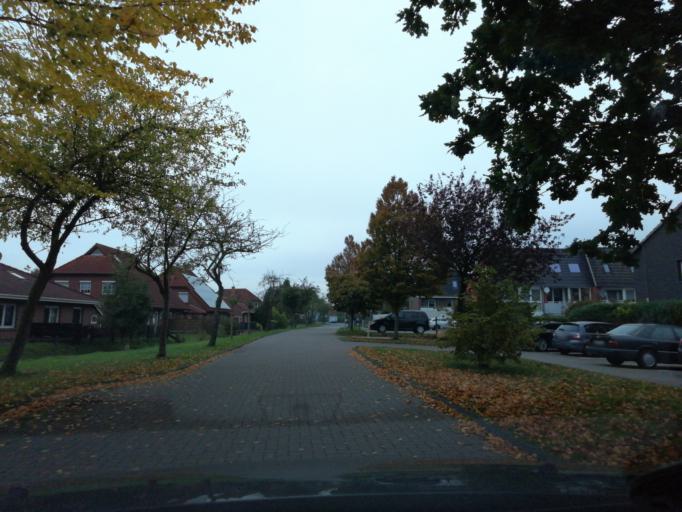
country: DE
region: Lower Saxony
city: Schillig
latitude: 53.6334
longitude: 8.0343
